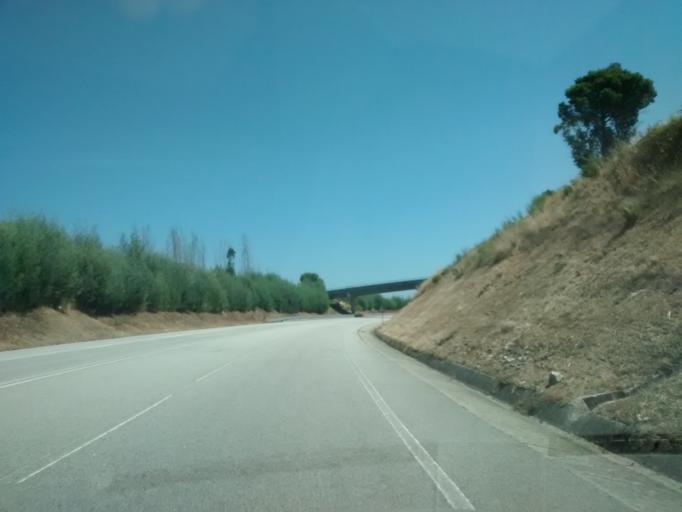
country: PT
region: Coimbra
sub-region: Tabua
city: Tabua
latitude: 40.3712
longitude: -8.0384
